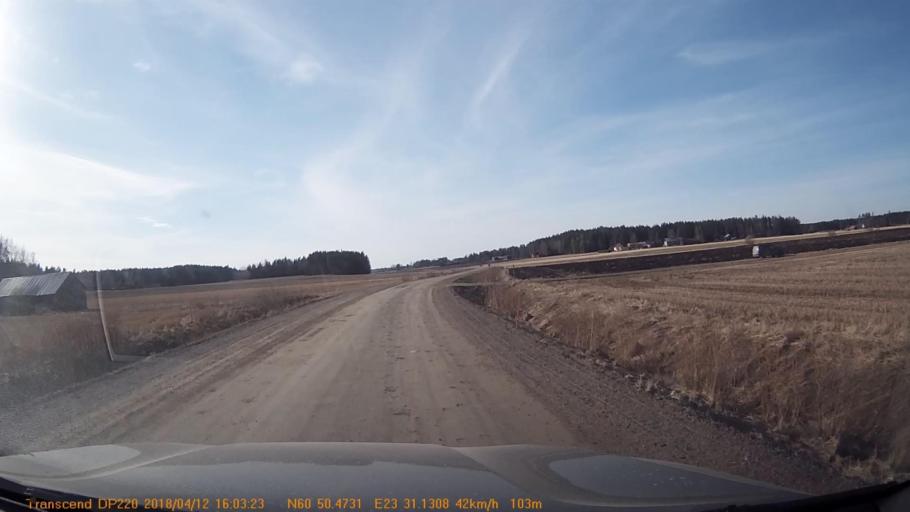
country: FI
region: Haeme
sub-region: Forssa
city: Jokioinen
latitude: 60.8413
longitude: 23.5185
